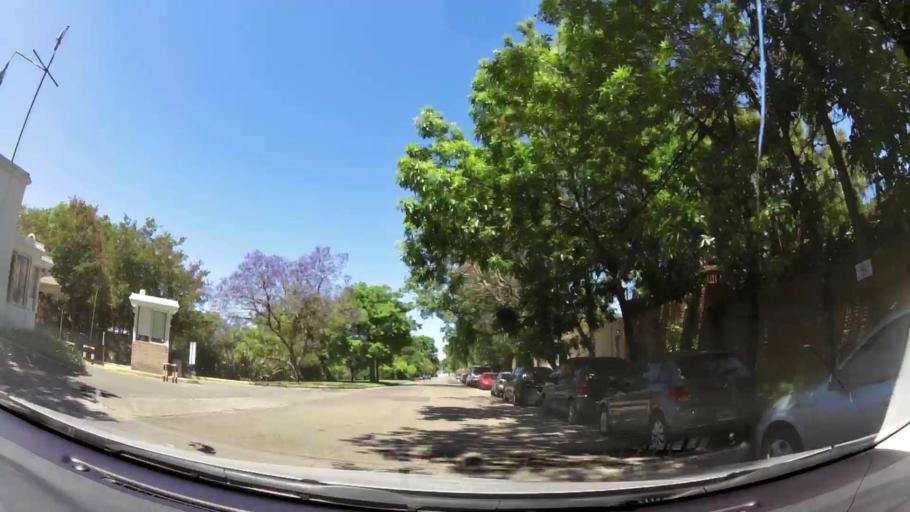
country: AR
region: Buenos Aires
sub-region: Partido de San Isidro
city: San Isidro
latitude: -34.4549
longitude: -58.5110
